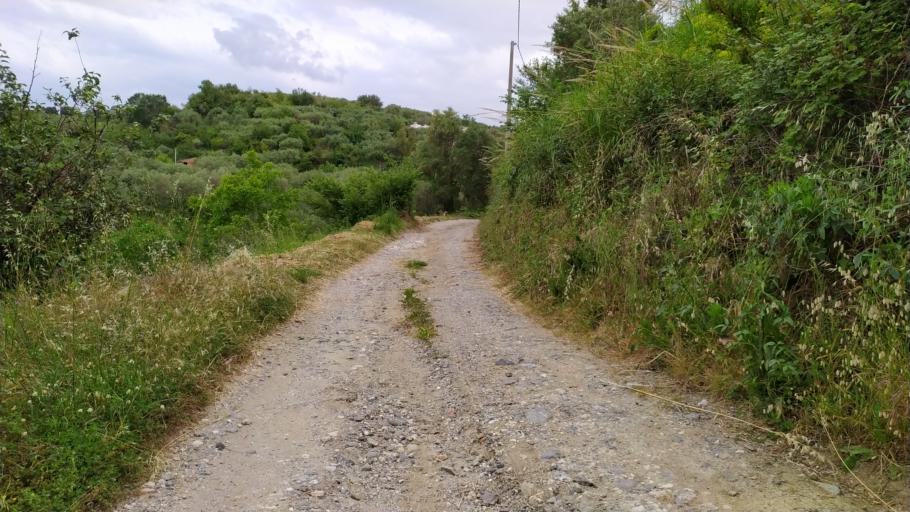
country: IT
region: Sicily
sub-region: Messina
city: Gualtieri Sicamino
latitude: 38.1554
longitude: 15.2997
